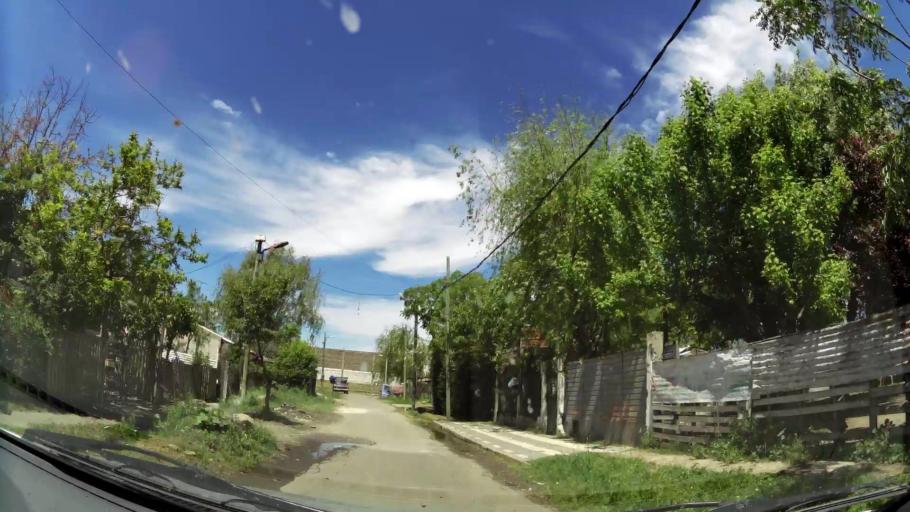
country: AR
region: Buenos Aires
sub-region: Partido de Quilmes
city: Quilmes
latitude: -34.7498
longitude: -58.3108
